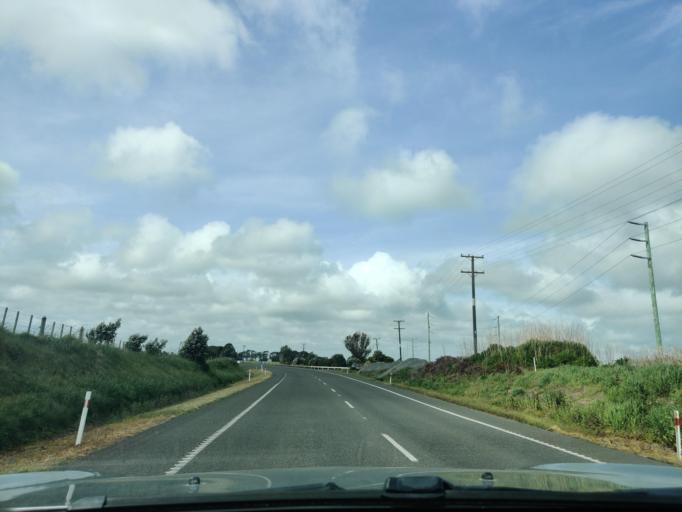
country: NZ
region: Taranaki
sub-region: South Taranaki District
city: Patea
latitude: -39.7720
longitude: 174.5935
